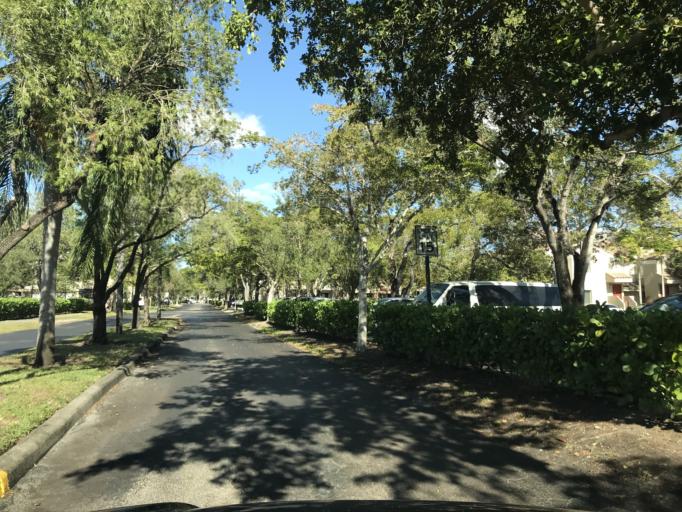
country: US
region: Florida
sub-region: Broward County
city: Pine Island Ridge
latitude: 26.1299
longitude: -80.2675
